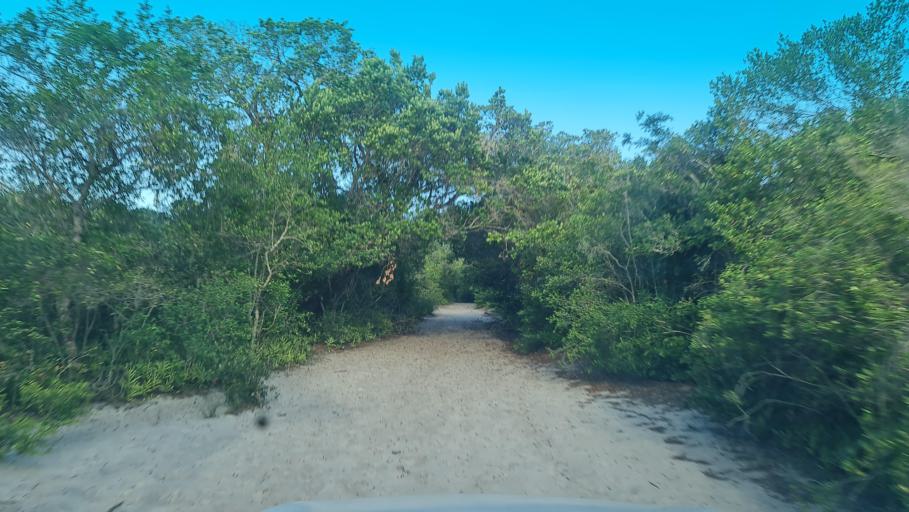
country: MZ
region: Gaza
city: Macia
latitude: -25.2277
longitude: 33.0202
